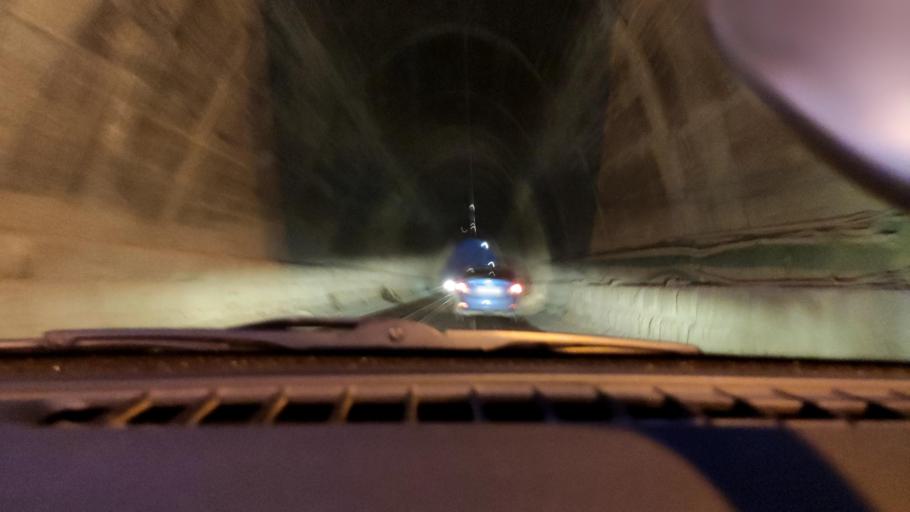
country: RU
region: Perm
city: Kondratovo
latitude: 58.0055
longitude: 56.1631
